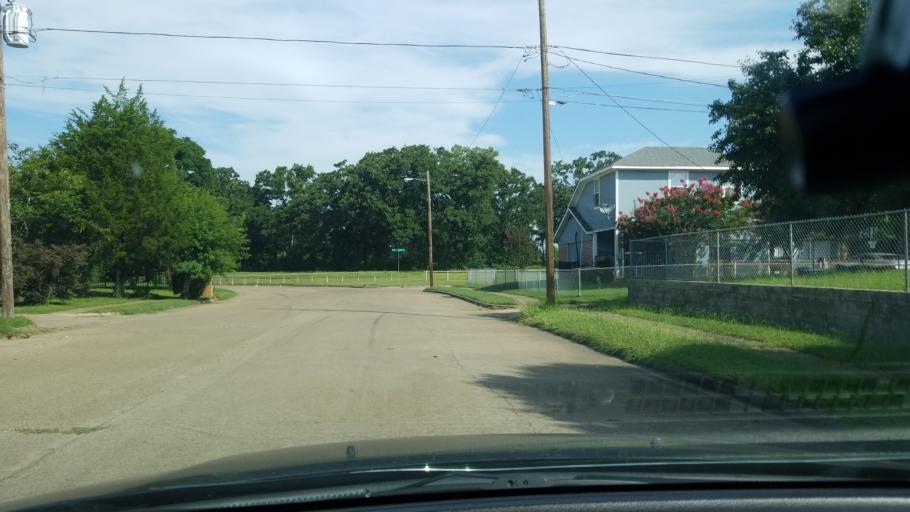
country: US
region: Texas
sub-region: Dallas County
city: Balch Springs
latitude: 32.7258
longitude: -96.6434
